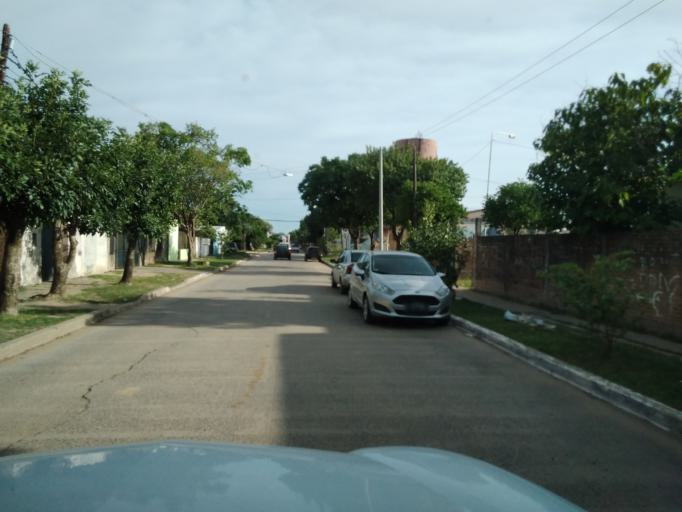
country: AR
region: Corrientes
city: Corrientes
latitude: -27.4900
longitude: -58.8436
